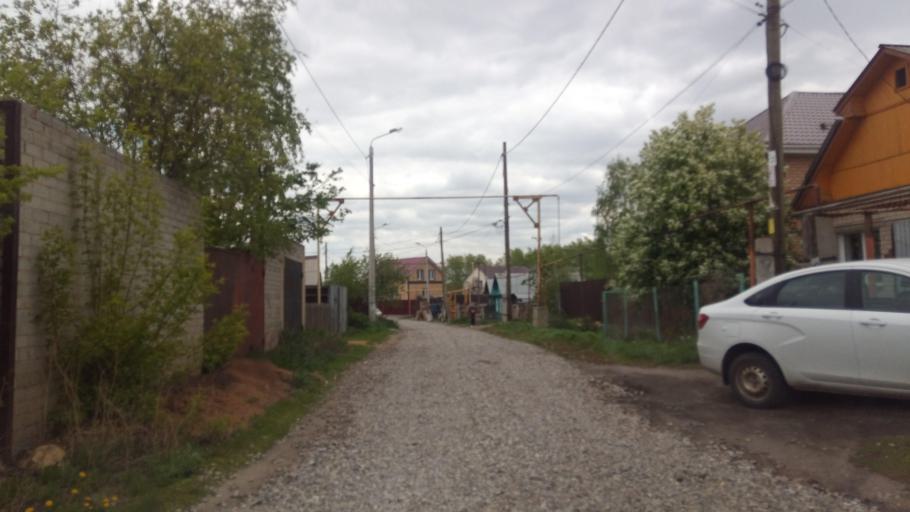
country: RU
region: Chelyabinsk
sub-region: Gorod Chelyabinsk
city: Chelyabinsk
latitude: 55.1274
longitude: 61.3985
